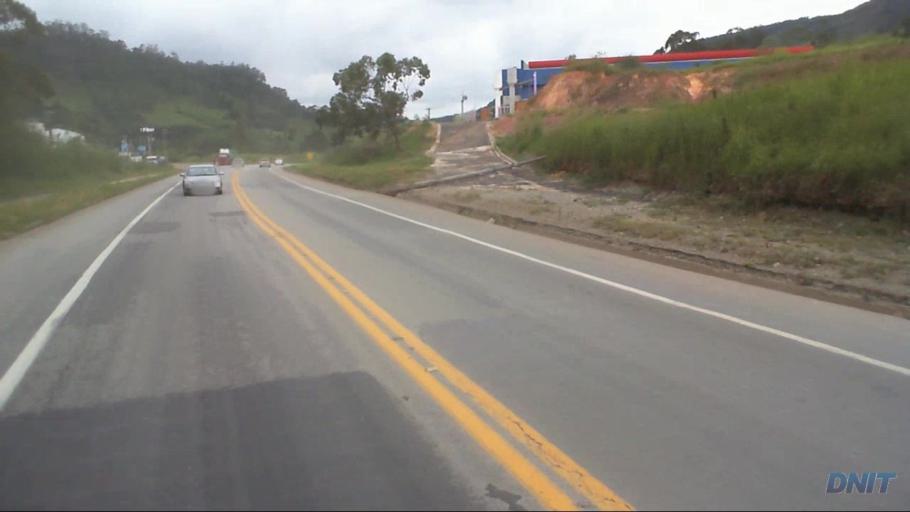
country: BR
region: Minas Gerais
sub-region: Joao Monlevade
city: Joao Monlevade
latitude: -19.8421
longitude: -43.1729
